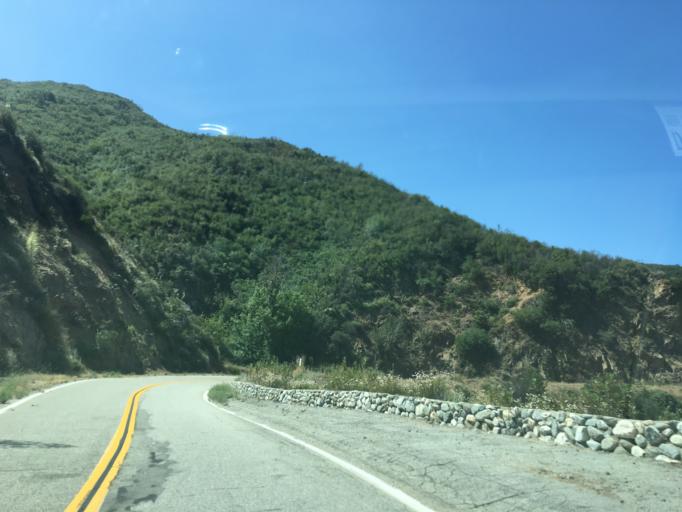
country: US
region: California
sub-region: Los Angeles County
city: Glendora
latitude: 34.2150
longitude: -117.7988
